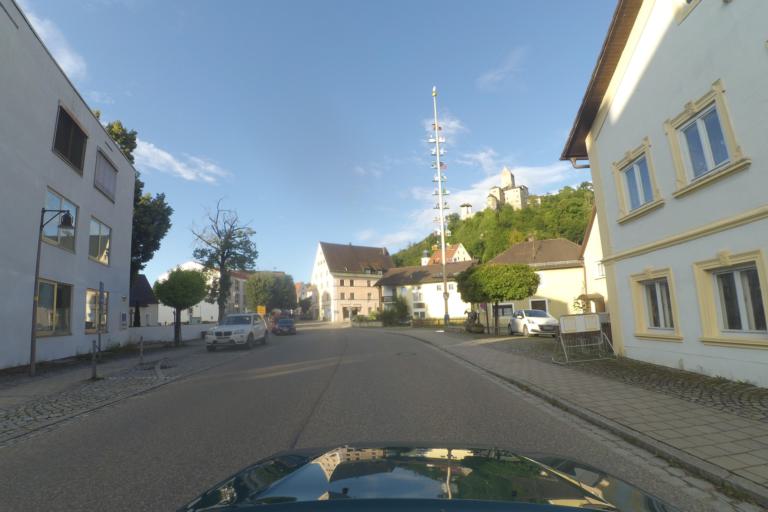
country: DE
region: Bavaria
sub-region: Upper Bavaria
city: Denkendorf
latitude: 48.9484
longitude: 11.3937
